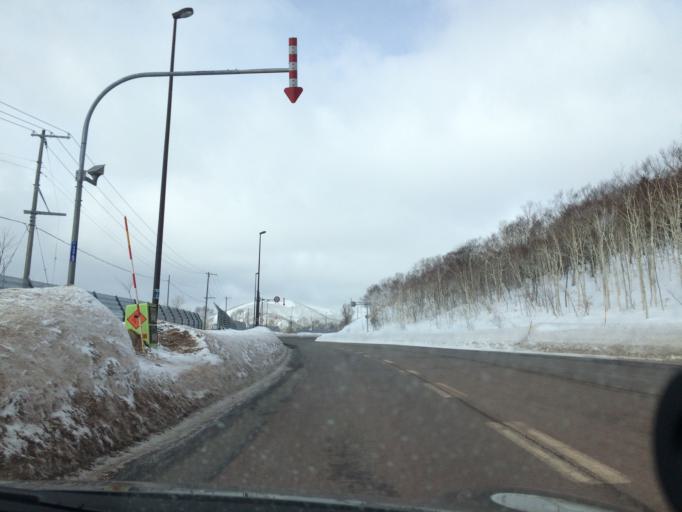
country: JP
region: Hokkaido
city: Shimo-furano
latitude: 43.1306
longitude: 142.7630
